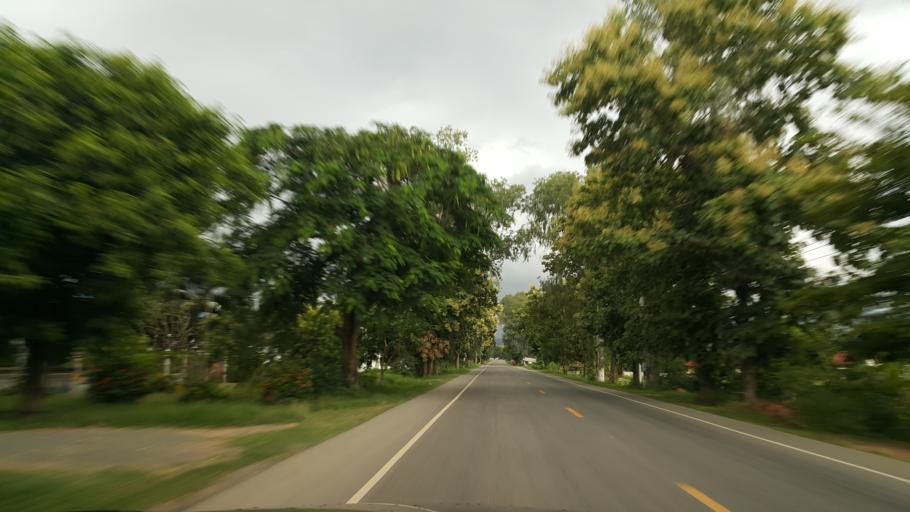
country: TH
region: Phayao
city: Dok Kham Tai
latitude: 19.2238
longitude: 100.0448
